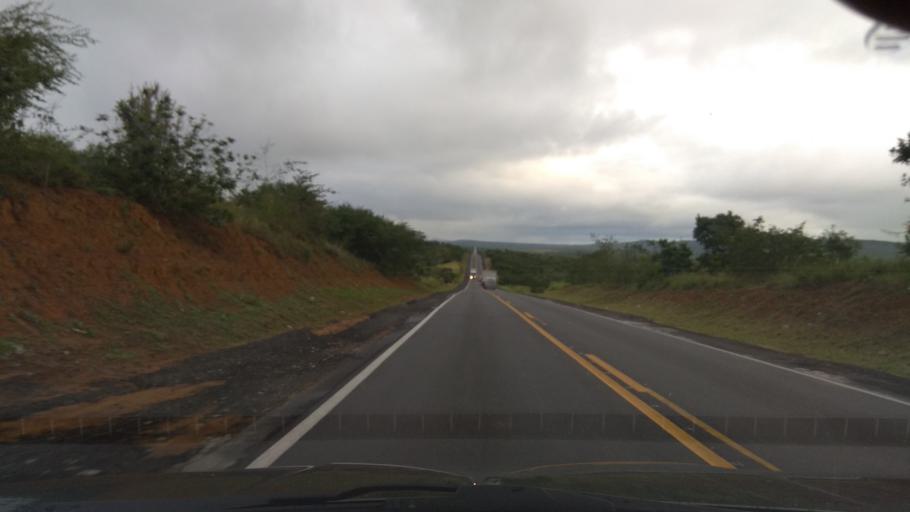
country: BR
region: Bahia
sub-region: Jaguaquara
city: Jaguaquara
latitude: -13.3843
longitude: -40.0211
